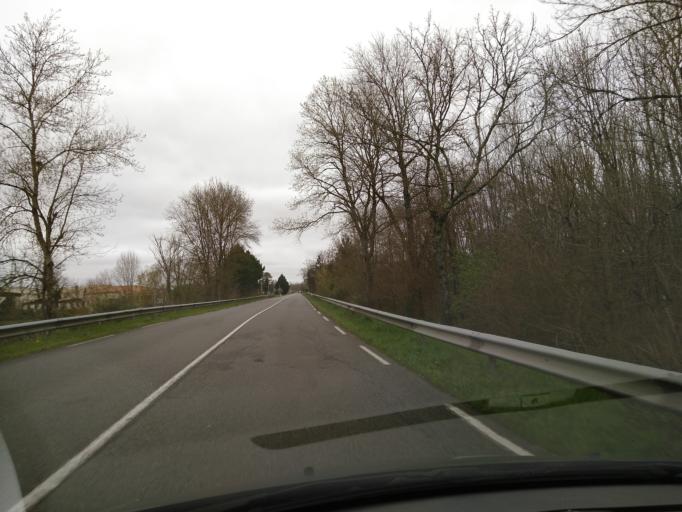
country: FR
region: Aquitaine
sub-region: Departement du Lot-et-Garonne
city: Castillonnes
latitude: 44.6726
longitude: 0.5799
